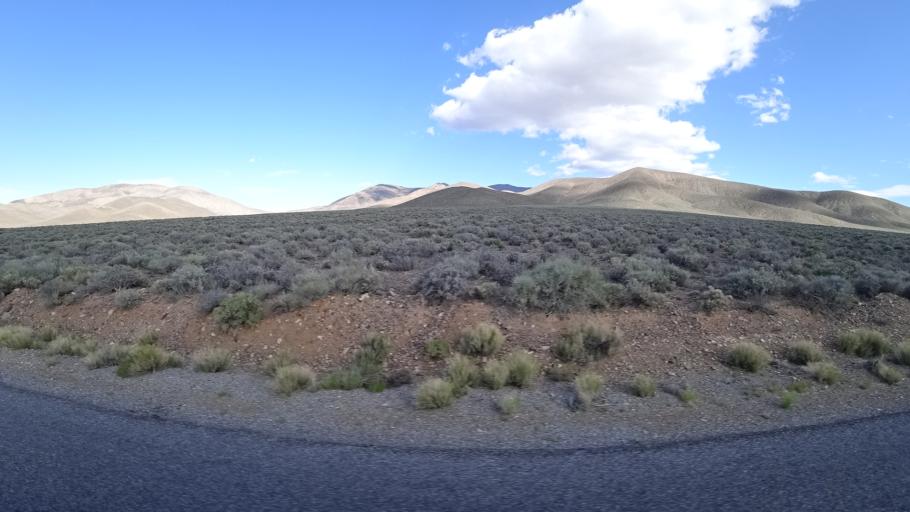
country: US
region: California
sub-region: San Bernardino County
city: Searles Valley
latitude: 36.3328
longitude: -117.1467
